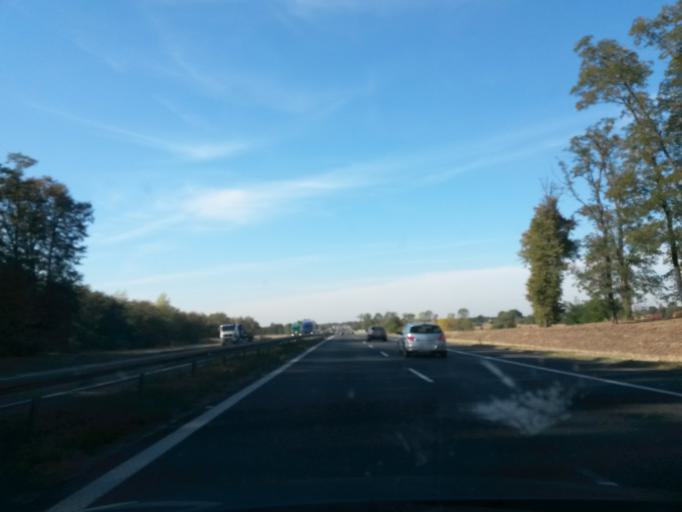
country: PL
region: Opole Voivodeship
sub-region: Powiat brzeski
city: Skarbimierz Osiedle
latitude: 50.7996
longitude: 17.3236
